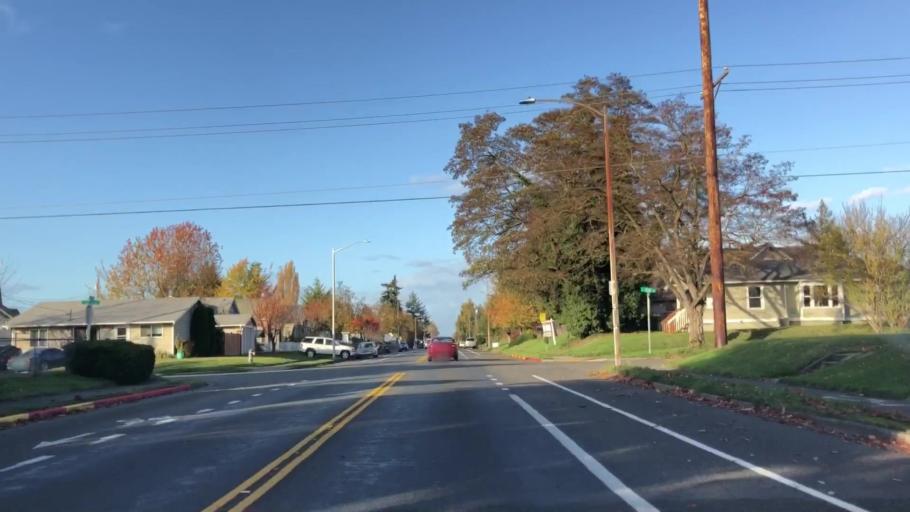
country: US
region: Washington
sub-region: Pierce County
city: Parkland
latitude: 47.2015
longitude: -122.4432
